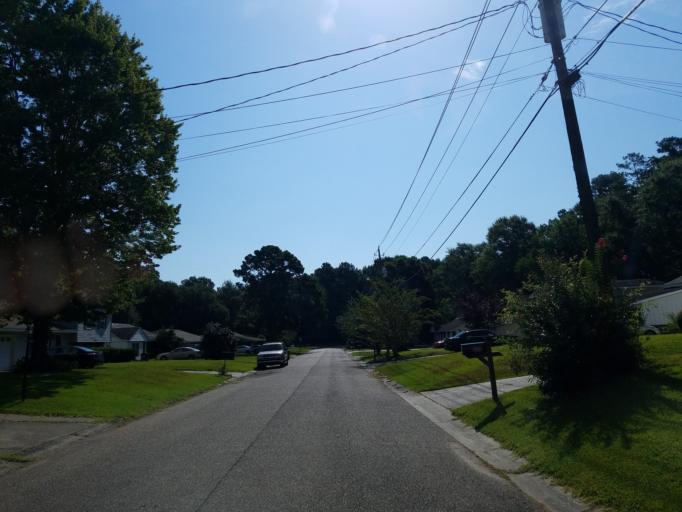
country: US
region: Mississippi
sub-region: Lamar County
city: West Hattiesburg
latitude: 31.3087
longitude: -89.3327
